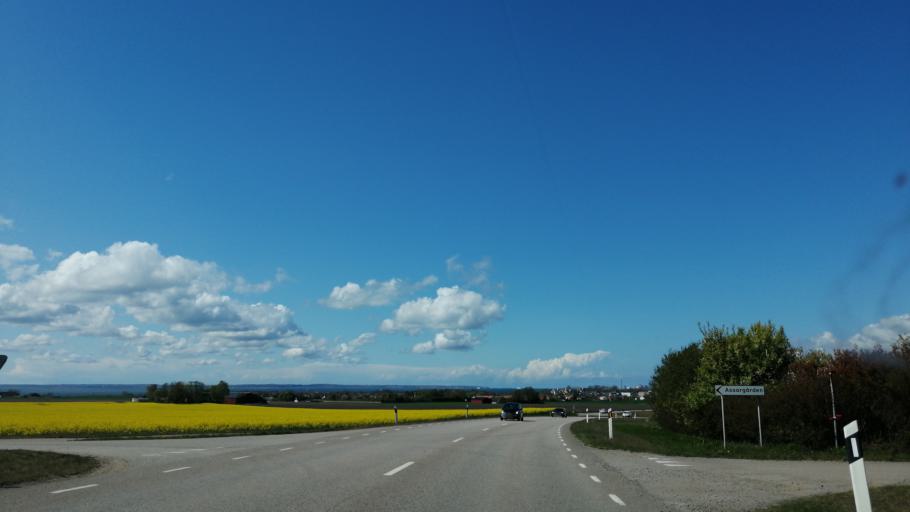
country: SE
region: Skane
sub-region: Helsingborg
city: Glumslov
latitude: 55.9521
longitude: 12.7975
